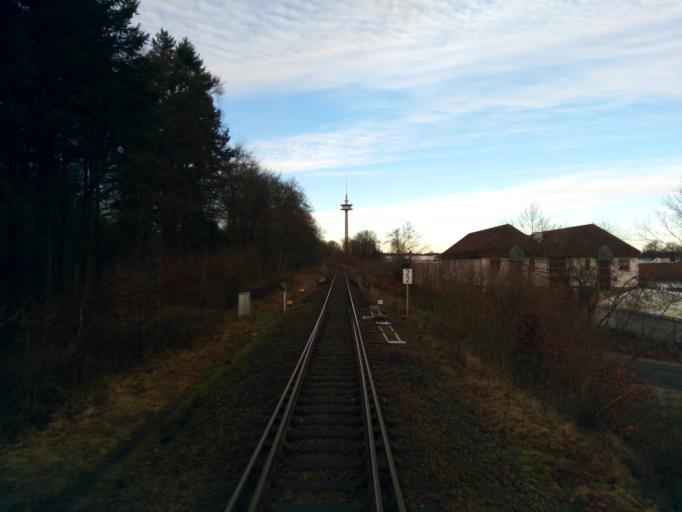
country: DE
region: Lower Saxony
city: Uelzen
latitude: 52.9861
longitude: 10.5422
